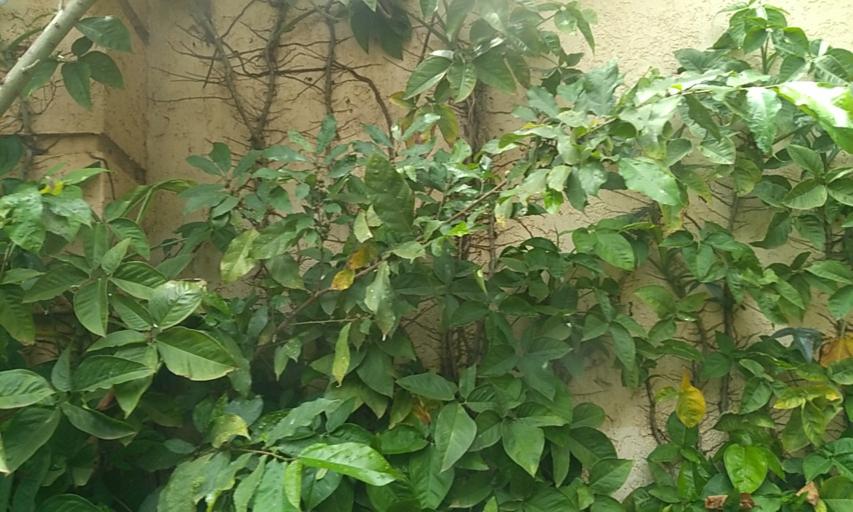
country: UG
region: Central Region
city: Kampala Central Division
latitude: 0.3329
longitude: 32.5917
